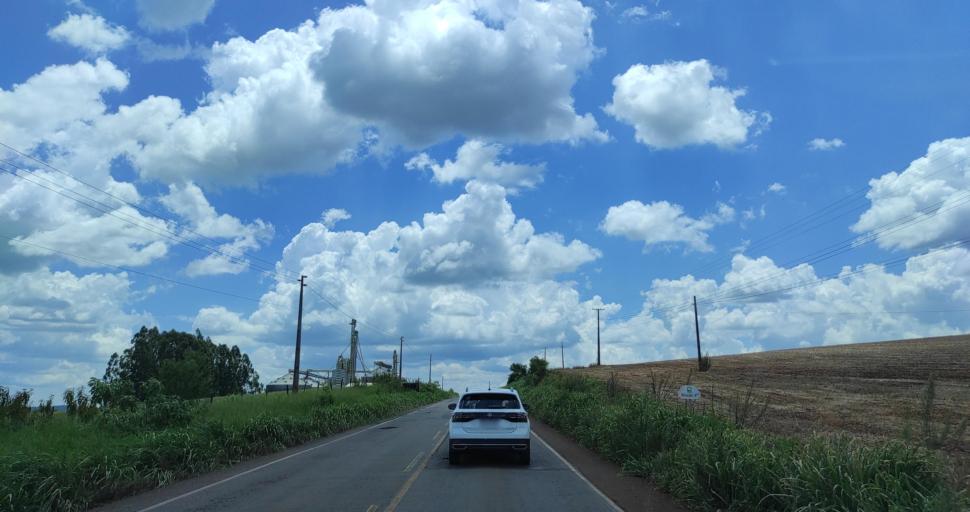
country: BR
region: Santa Catarina
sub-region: Xanxere
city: Xanxere
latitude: -26.7654
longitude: -52.4048
